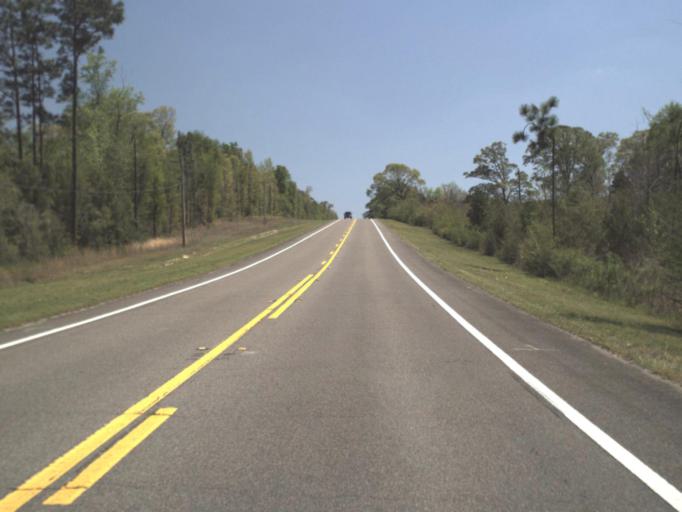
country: US
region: Alabama
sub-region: Escambia County
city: East Brewton
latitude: 30.9425
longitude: -87.0678
